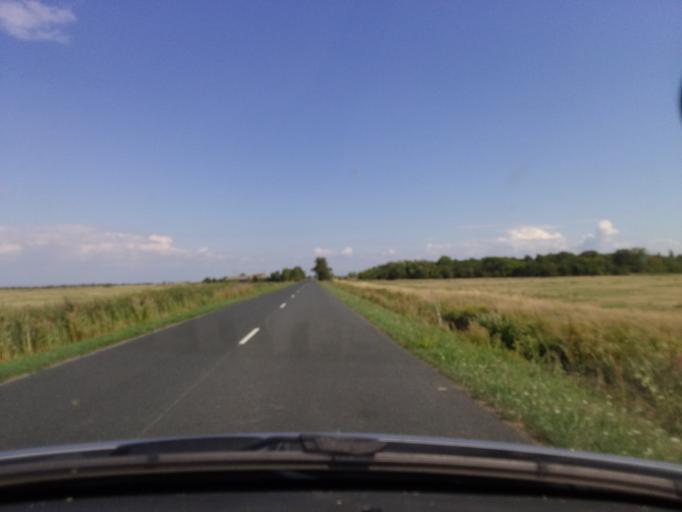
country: FR
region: Pays de la Loire
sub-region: Departement de la Vendee
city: Triaize
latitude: 46.4003
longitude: -1.2360
